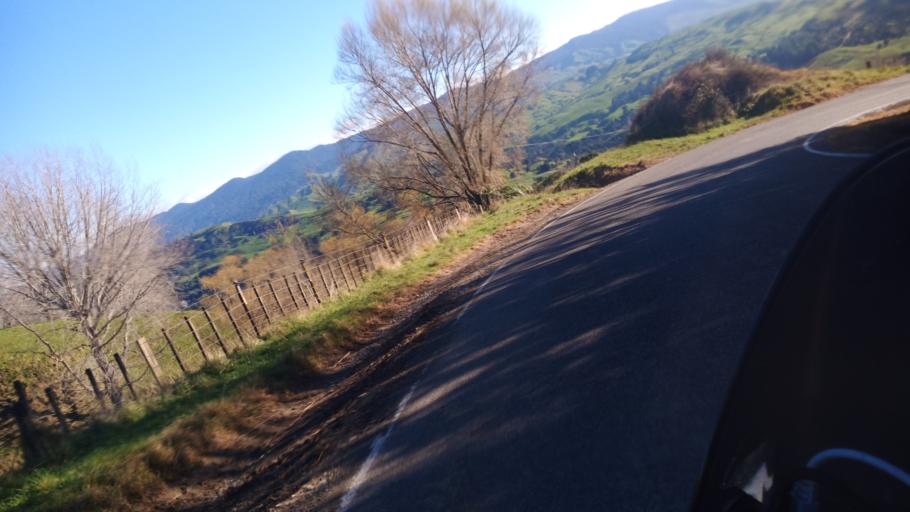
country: NZ
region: Hawke's Bay
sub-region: Wairoa District
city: Wairoa
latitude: -38.8272
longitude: 177.2903
